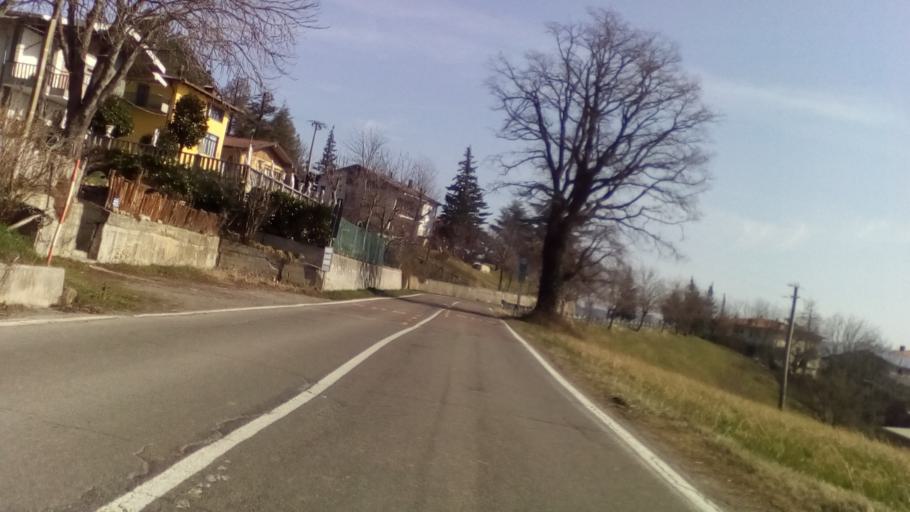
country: IT
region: Emilia-Romagna
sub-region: Provincia di Modena
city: Lama
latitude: 44.3111
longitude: 10.7774
